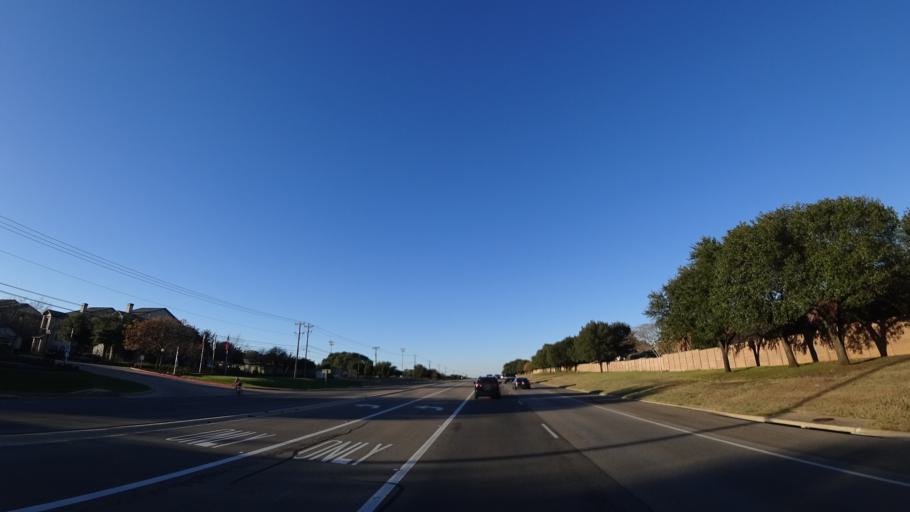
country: US
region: Texas
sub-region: Williamson County
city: Brushy Creek
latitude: 30.4894
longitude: -97.7718
